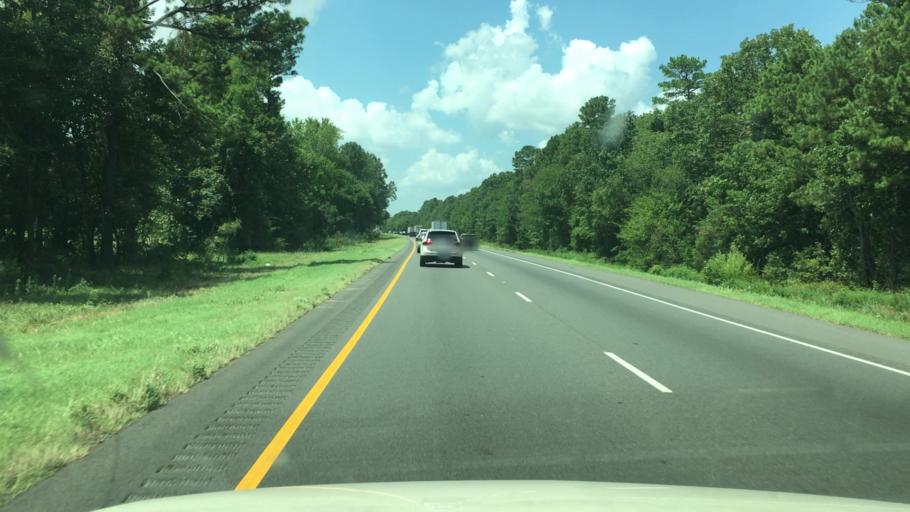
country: US
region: Arkansas
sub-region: Hempstead County
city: Hope
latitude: 33.7178
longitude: -93.5612
